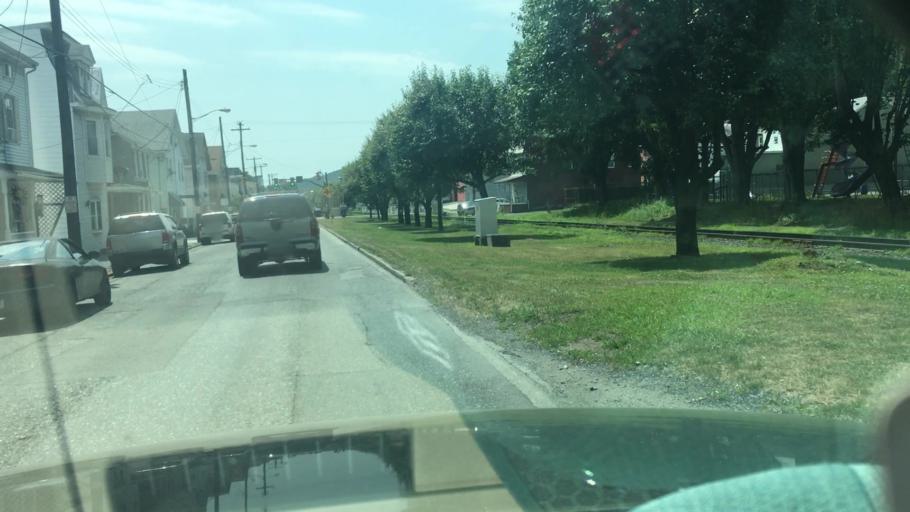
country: US
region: Pennsylvania
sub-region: Schuylkill County
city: Tamaqua
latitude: 40.8029
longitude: -75.9710
